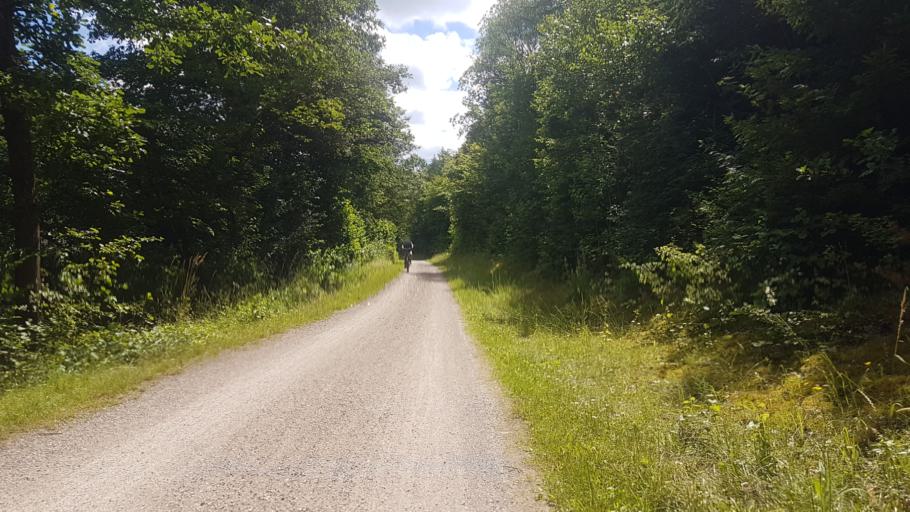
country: DE
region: Bavaria
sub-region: Regierungsbezirk Mittelfranken
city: Gunzenhausen
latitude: 49.1280
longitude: 10.7858
